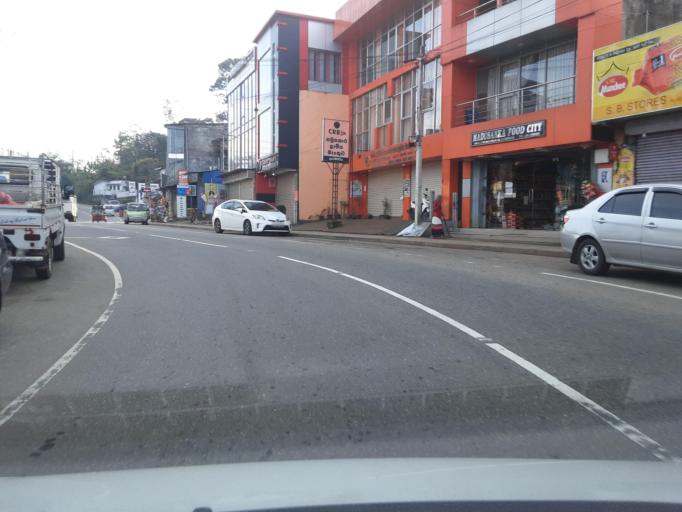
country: LK
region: Uva
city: Badulla
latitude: 6.9360
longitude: 80.9893
